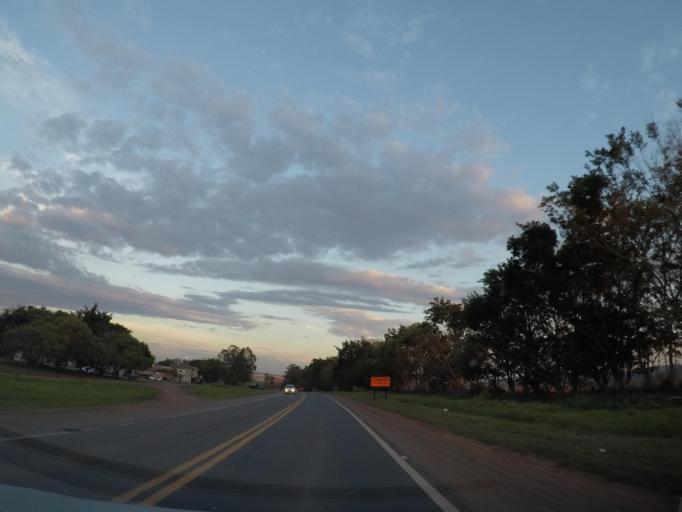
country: BR
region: Sao Paulo
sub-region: Indaiatuba
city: Indaiatuba
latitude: -23.0439
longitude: -47.1066
